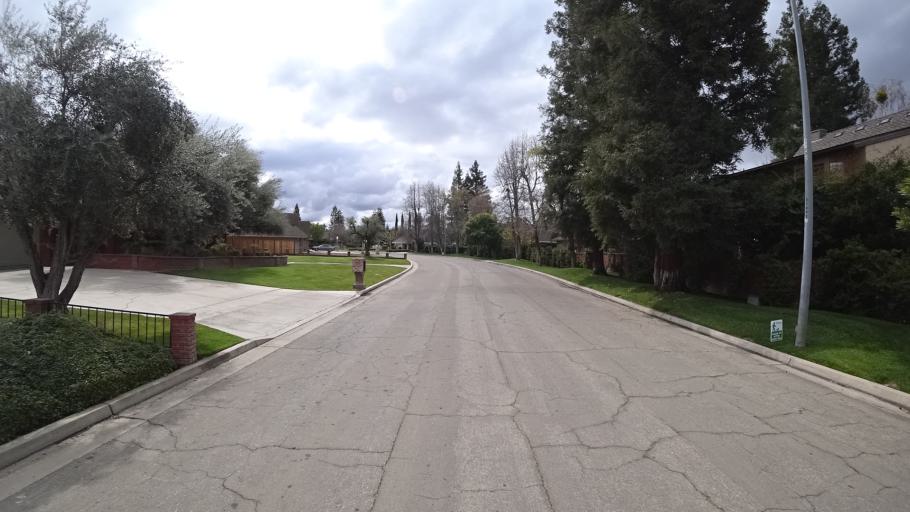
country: US
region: California
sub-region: Fresno County
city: Fresno
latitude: 36.8467
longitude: -119.8371
